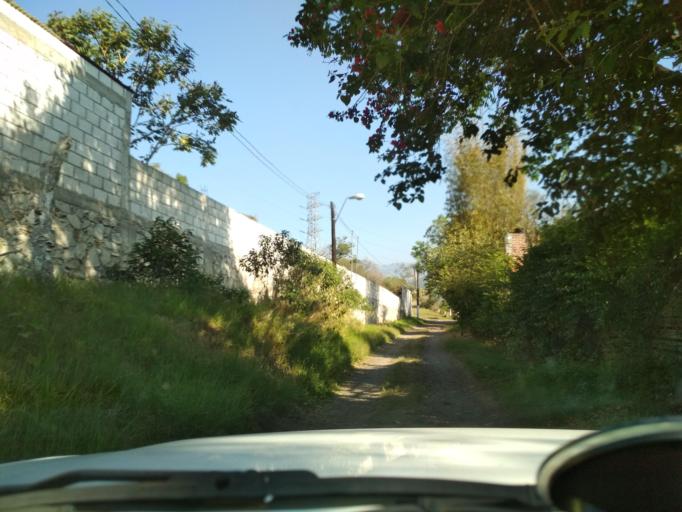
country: MX
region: Veracruz
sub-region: Nogales
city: Agricola Lazaro Cardenas
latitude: 18.8066
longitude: -97.2012
